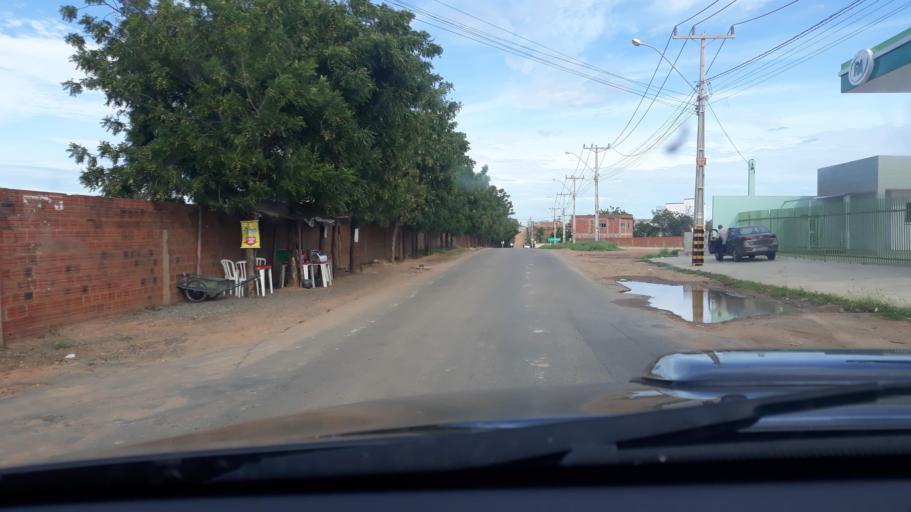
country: BR
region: Bahia
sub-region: Guanambi
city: Guanambi
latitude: -14.2065
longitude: -42.7936
